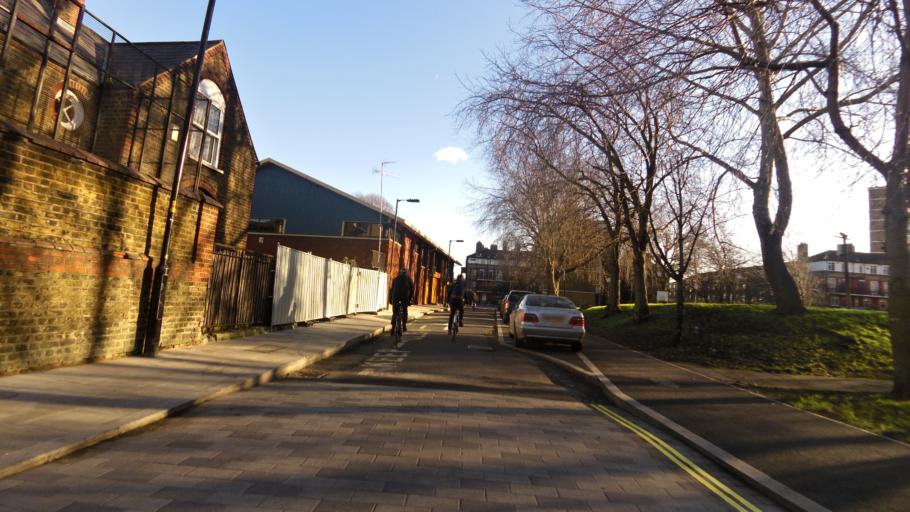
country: GB
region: England
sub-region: Greater London
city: City of London
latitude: 51.4956
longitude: -0.0823
